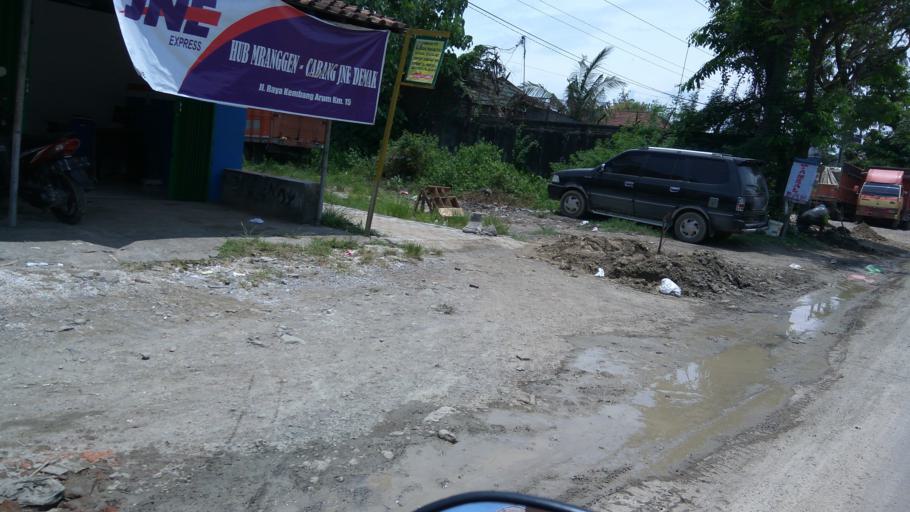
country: ID
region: Central Java
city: Mranggen
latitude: -7.0302
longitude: 110.5348
